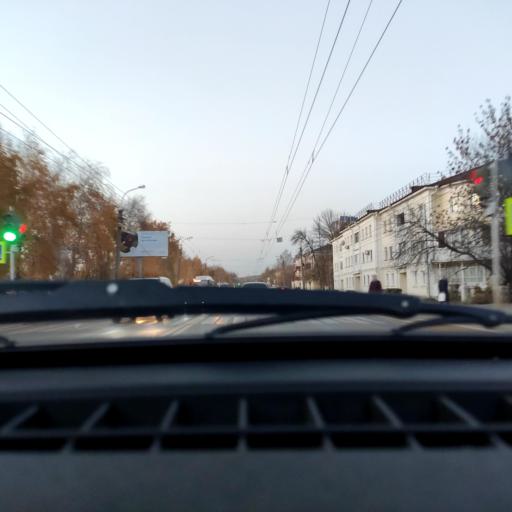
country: RU
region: Bashkortostan
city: Ufa
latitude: 54.7928
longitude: 56.1393
